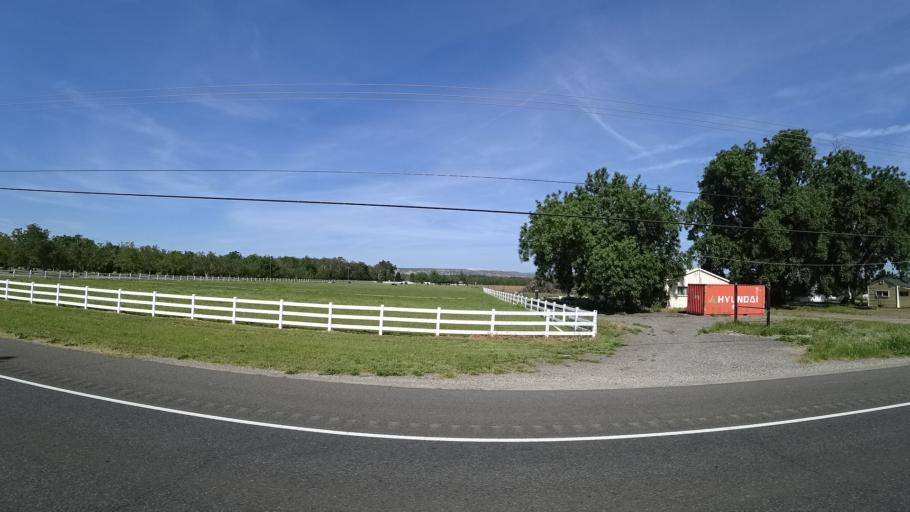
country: US
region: California
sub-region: Tehama County
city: Red Bluff
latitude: 40.1597
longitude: -122.1493
